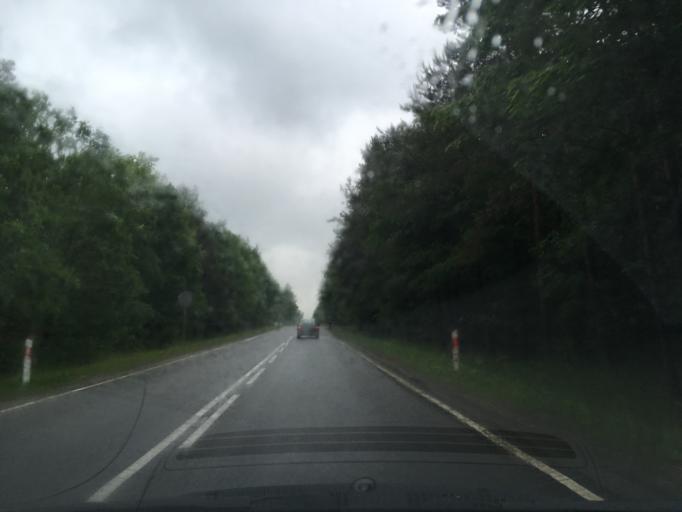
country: PL
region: Lublin Voivodeship
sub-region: Powiat rycki
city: Ryki
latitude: 51.5802
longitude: 21.9140
